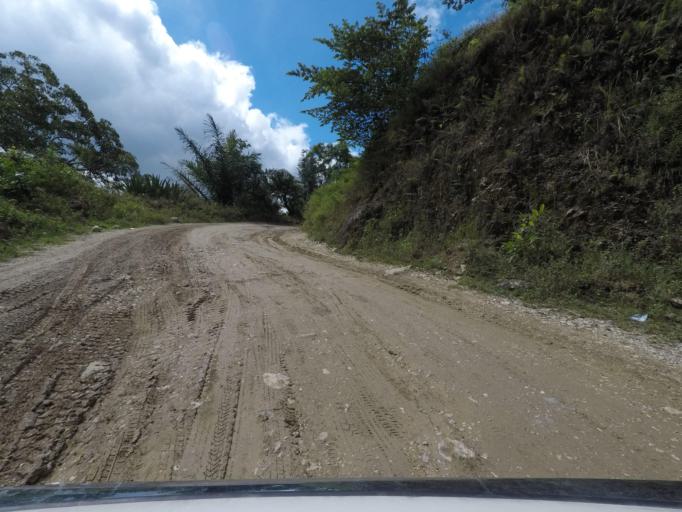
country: TL
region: Baucau
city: Venilale
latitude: -8.7183
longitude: 126.3668
